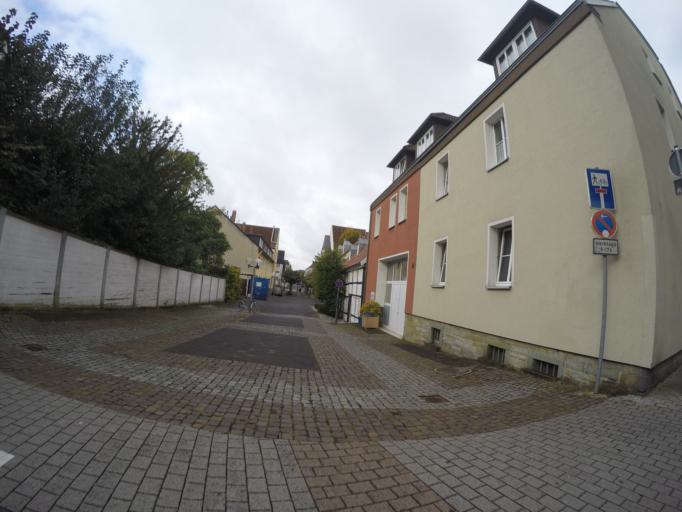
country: DE
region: North Rhine-Westphalia
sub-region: Regierungsbezirk Arnsberg
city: Lippstadt
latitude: 51.6744
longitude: 8.3505
